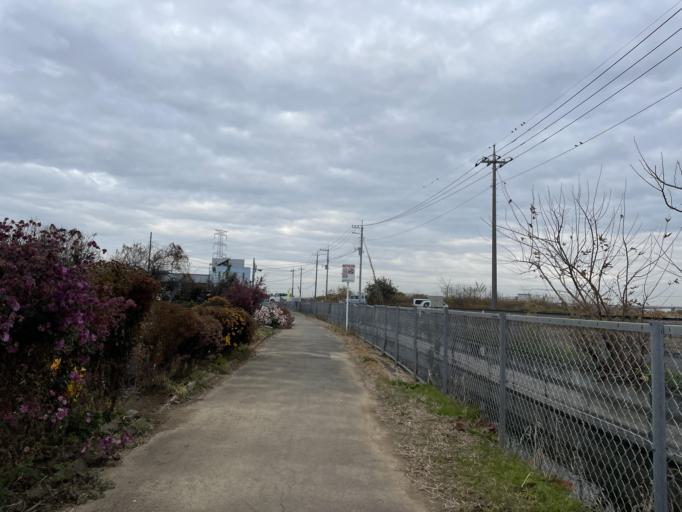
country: JP
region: Saitama
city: Shiraoka
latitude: 36.0327
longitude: 139.6572
